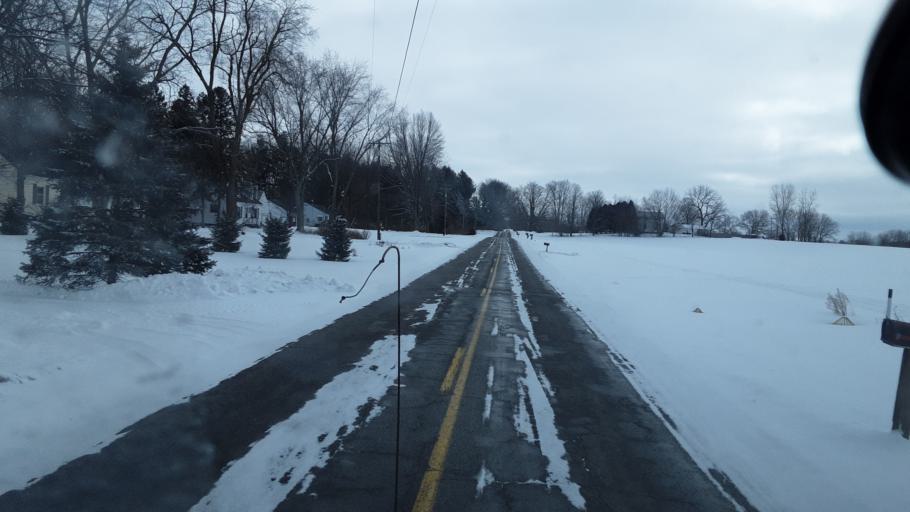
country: US
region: Michigan
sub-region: Ingham County
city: Holt
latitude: 42.5968
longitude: -84.5377
